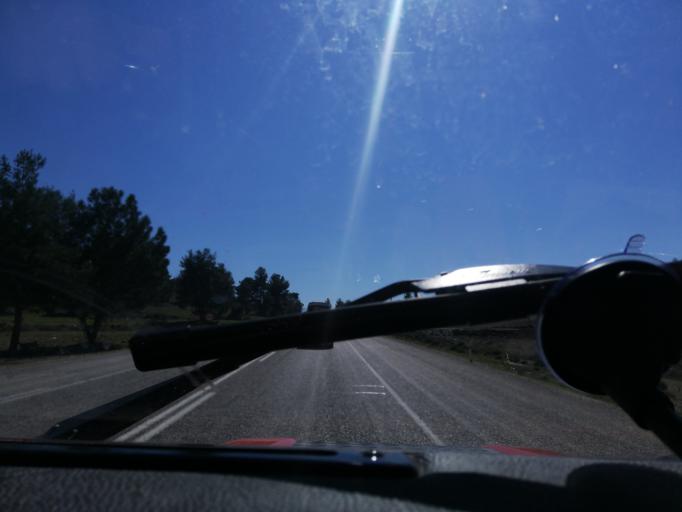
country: TR
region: Mugla
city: Kemer
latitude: 36.6119
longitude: 29.3581
